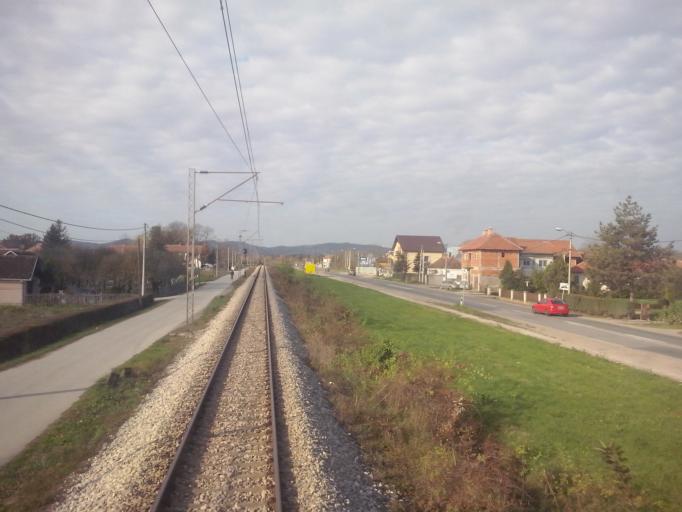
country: RS
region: Central Serbia
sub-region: Kolubarski Okrug
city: Lajkovac
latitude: 44.3647
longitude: 20.1460
